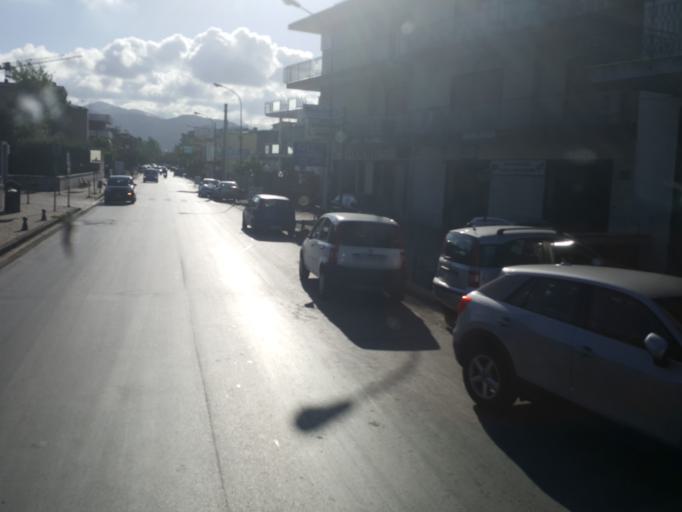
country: IT
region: Campania
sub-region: Provincia di Napoli
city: Nola
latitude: 40.9172
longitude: 14.5208
